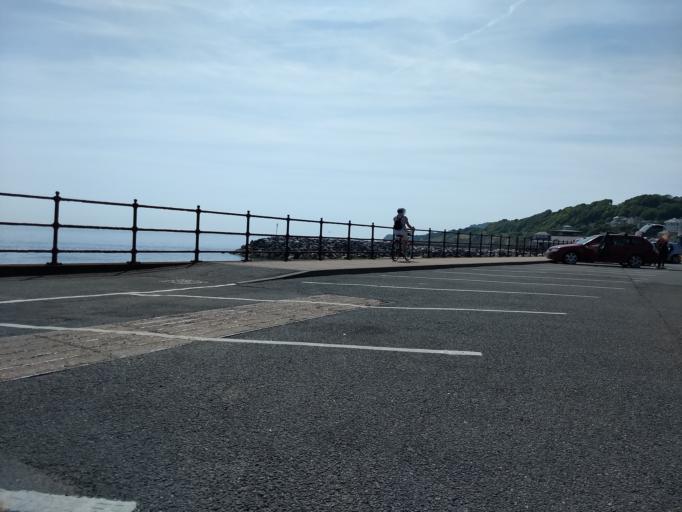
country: GB
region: England
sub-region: Isle of Wight
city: Ventnor
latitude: 50.5930
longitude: -1.2020
